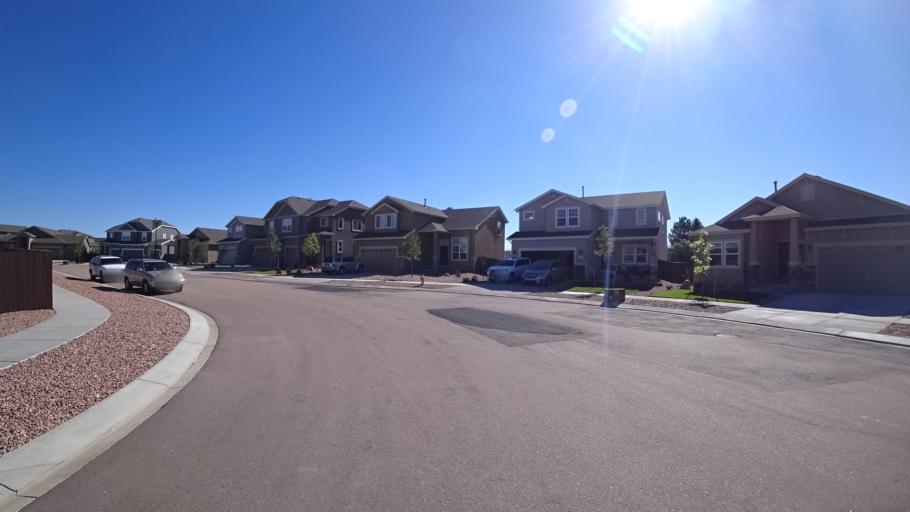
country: US
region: Colorado
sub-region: El Paso County
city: Black Forest
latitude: 38.9448
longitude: -104.6741
